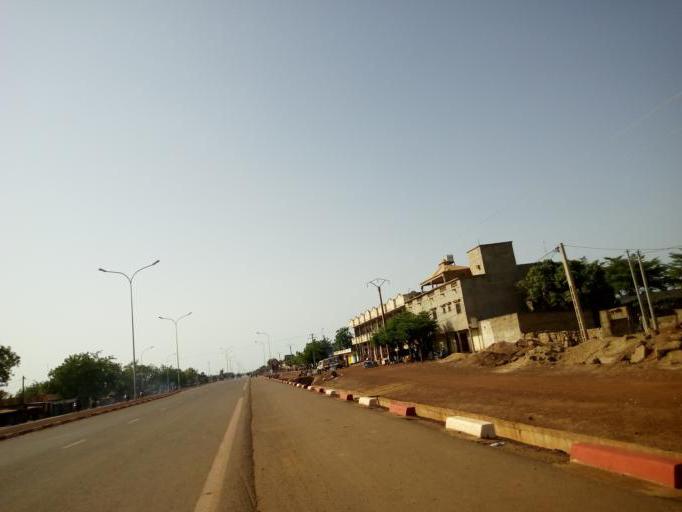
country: ML
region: Segou
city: Segou
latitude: 13.4302
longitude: -6.2239
